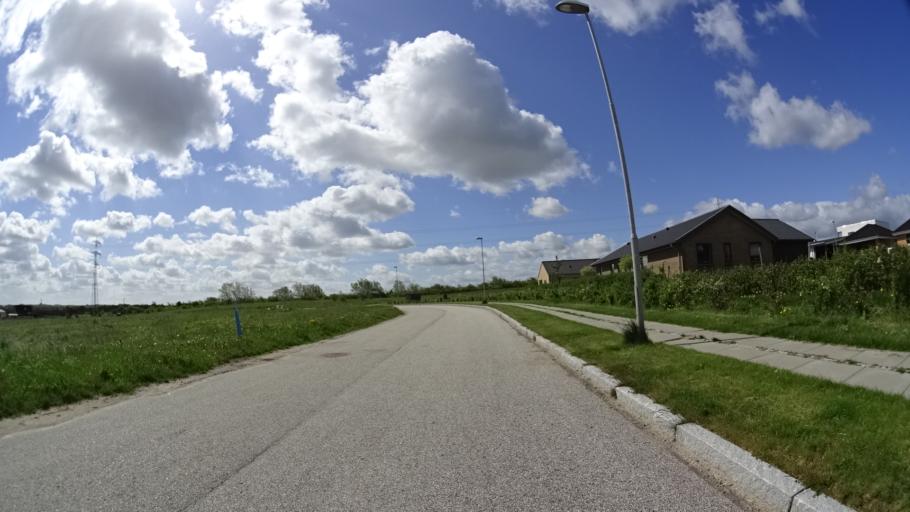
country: DK
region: Central Jutland
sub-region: Arhus Kommune
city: Stavtrup
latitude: 56.1268
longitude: 10.1115
